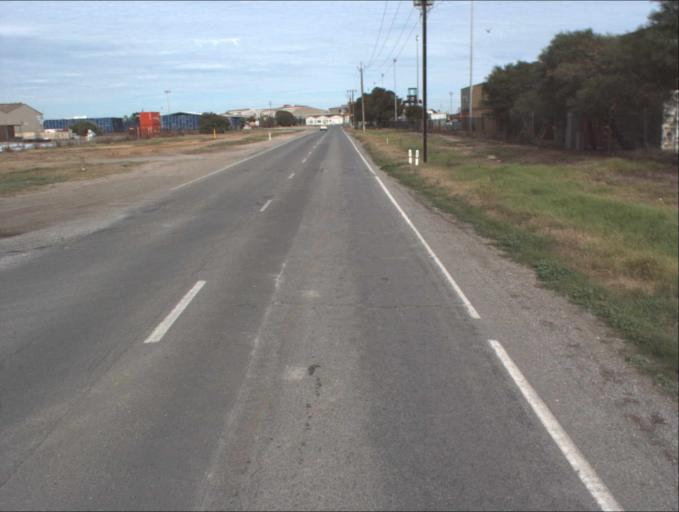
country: AU
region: South Australia
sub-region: Port Adelaide Enfield
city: Birkenhead
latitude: -34.8300
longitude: 138.5180
